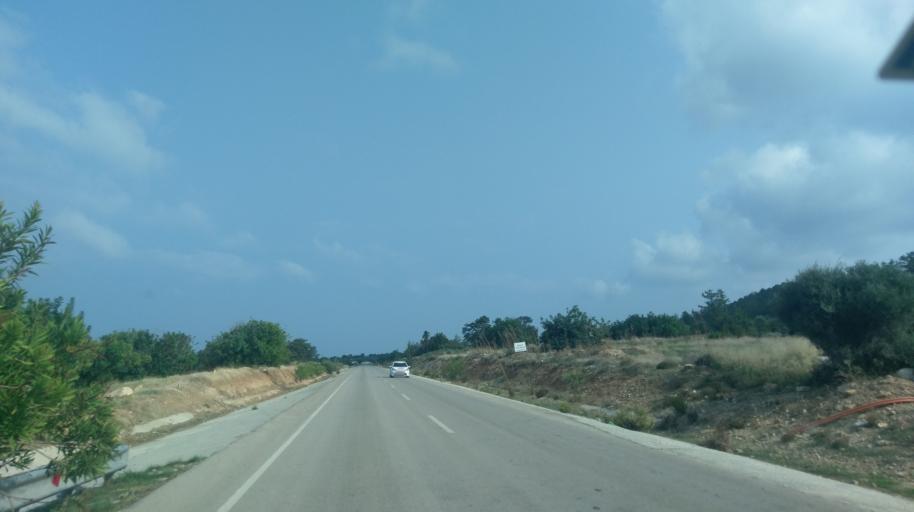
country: CY
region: Ammochostos
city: Lefkonoiko
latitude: 35.3754
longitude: 33.7151
